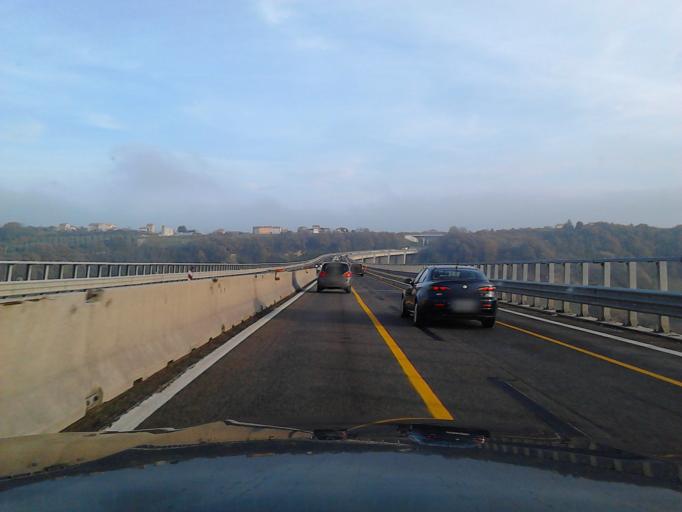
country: IT
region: Abruzzo
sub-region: Provincia di Chieti
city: Ortona
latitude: 42.3135
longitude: 14.4124
